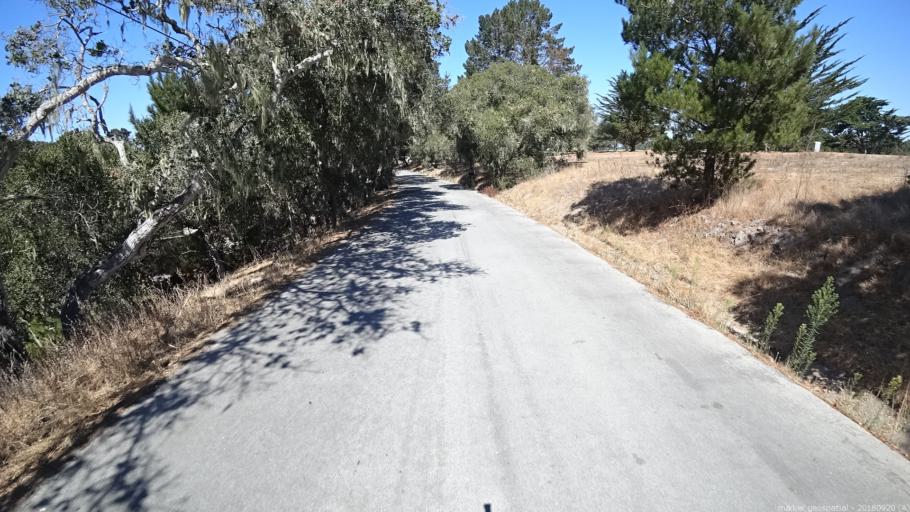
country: US
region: California
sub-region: Monterey County
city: Monterey
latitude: 36.5859
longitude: -121.8739
